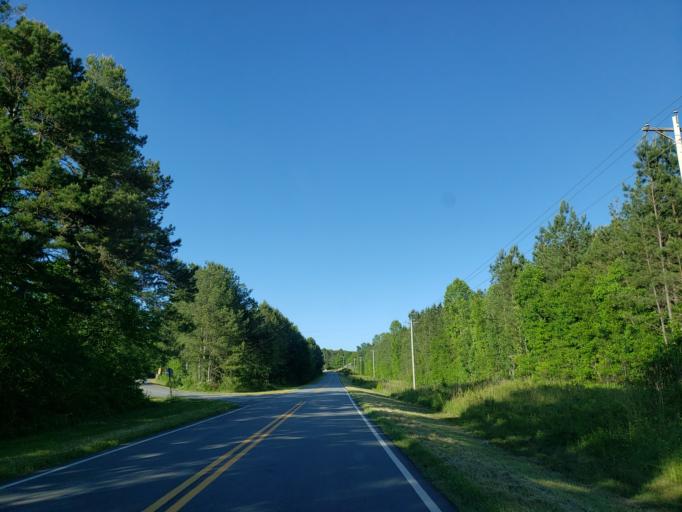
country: US
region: Georgia
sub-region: Haralson County
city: Buchanan
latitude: 33.7976
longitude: -85.2445
